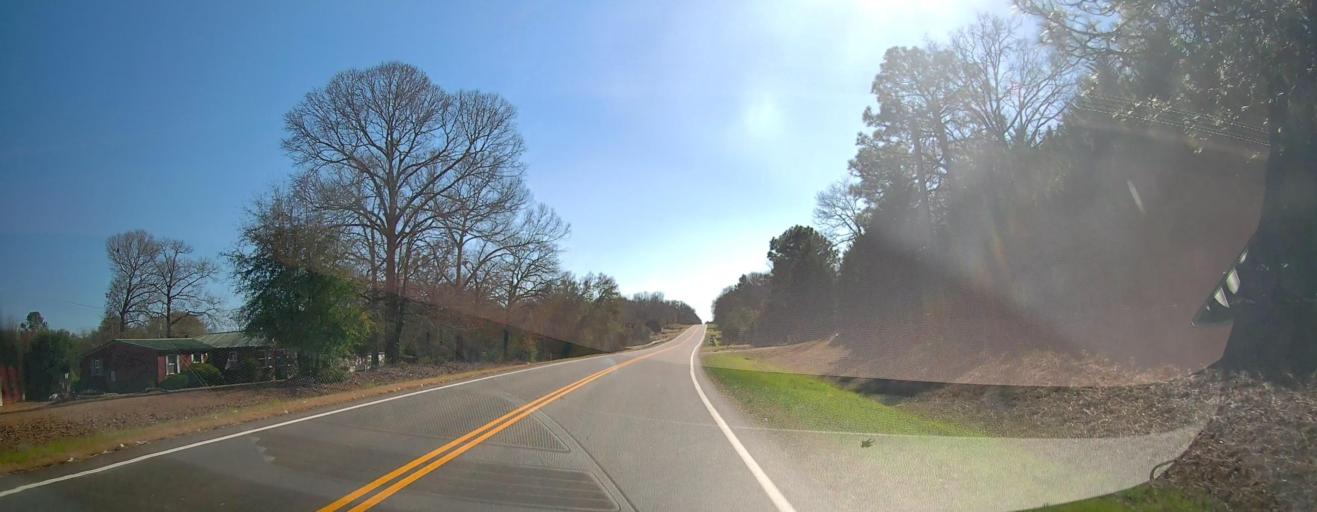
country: US
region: Georgia
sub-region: Macon County
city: Oglethorpe
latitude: 32.2515
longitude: -84.0862
